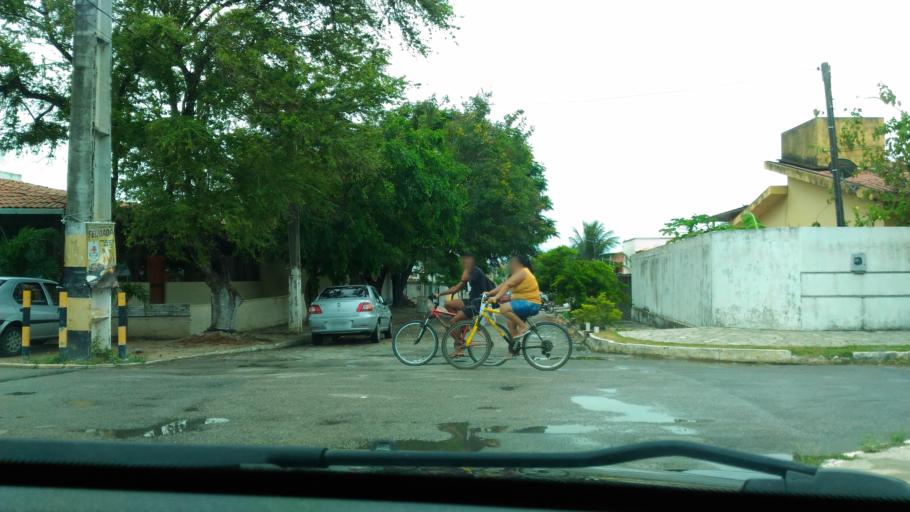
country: BR
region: Paraiba
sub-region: Joao Pessoa
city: Joao Pessoa
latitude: -7.1595
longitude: -34.8218
